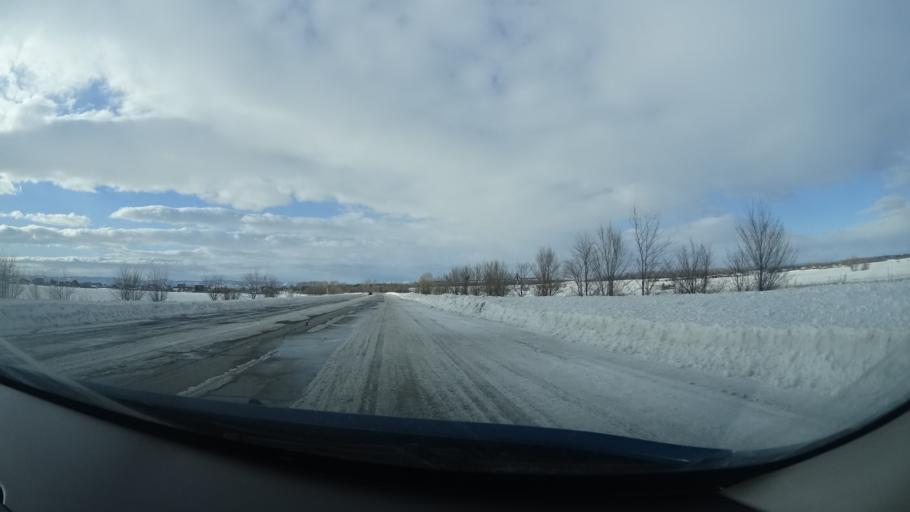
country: RU
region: Chelyabinsk
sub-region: Gorod Magnitogorsk
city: Magnitogorsk
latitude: 53.5882
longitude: 58.8792
